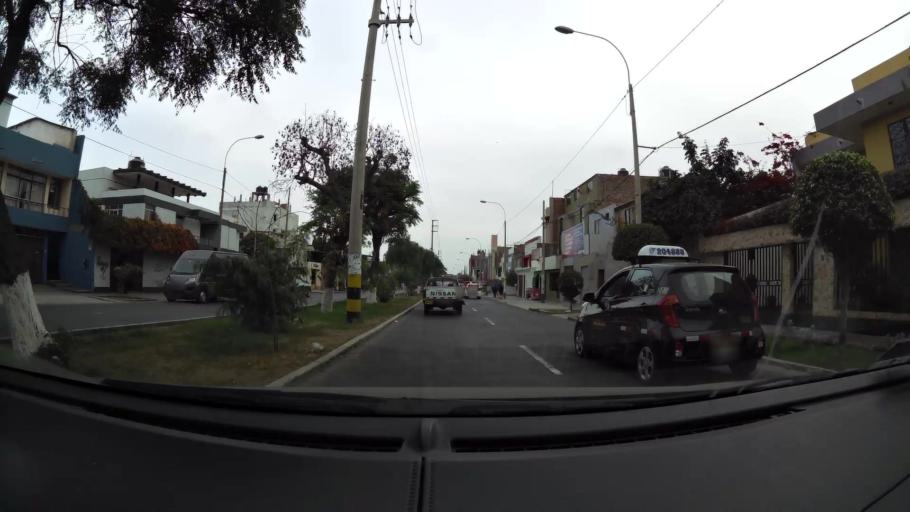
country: PE
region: La Libertad
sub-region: Provincia de Trujillo
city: Trujillo
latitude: -8.1011
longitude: -79.0321
